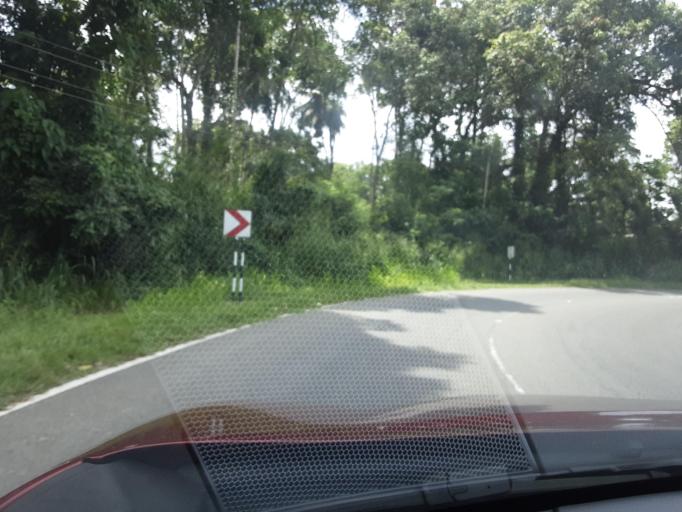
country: LK
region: Uva
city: Monaragala
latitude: 6.8974
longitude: 81.2756
